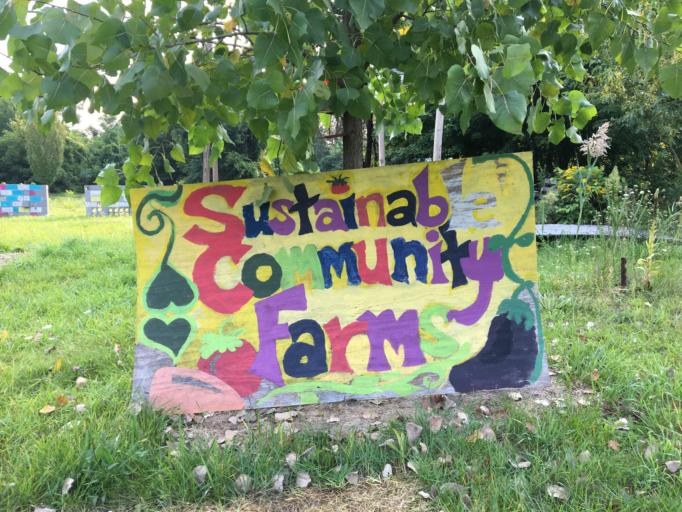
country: US
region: Michigan
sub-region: Wayne County
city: Grosse Pointe Park
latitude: 42.3954
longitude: -82.9842
